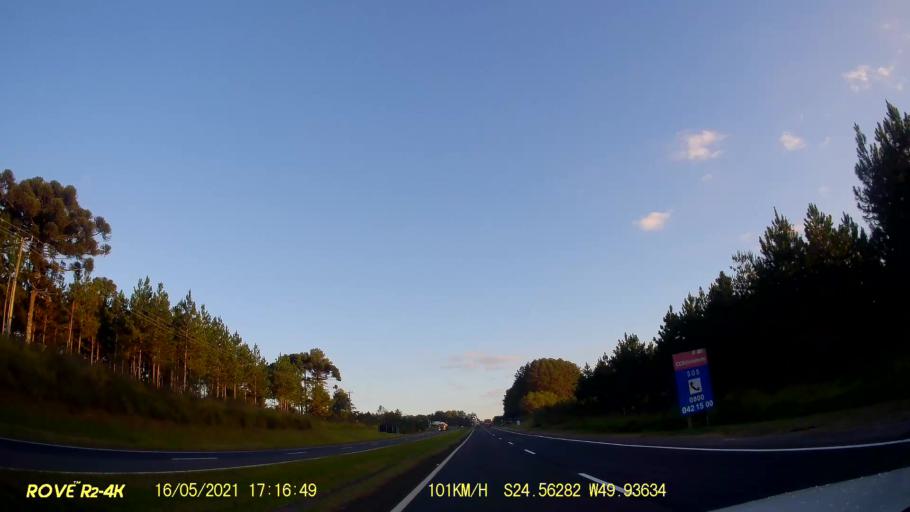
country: BR
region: Parana
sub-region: Pirai Do Sul
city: Pirai do Sul
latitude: -24.5632
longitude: -49.9364
